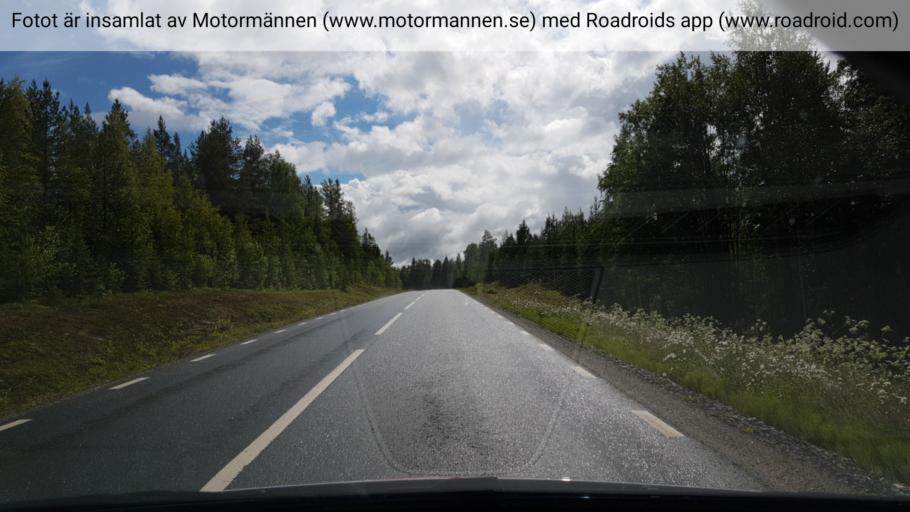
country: SE
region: Vaesterbotten
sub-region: Bjurholms Kommun
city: Bjurholm
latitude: 64.3651
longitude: 19.1408
